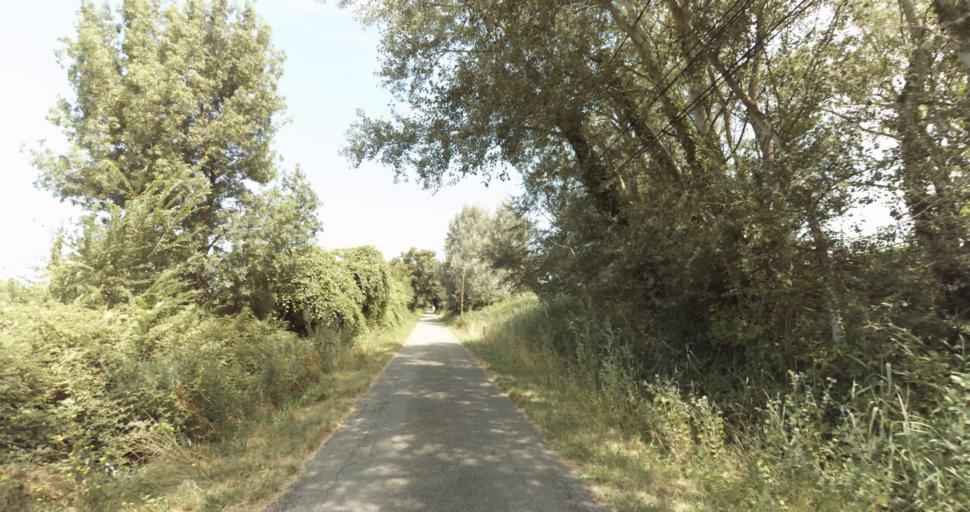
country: FR
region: Provence-Alpes-Cote d'Azur
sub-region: Departement du Vaucluse
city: Althen-des-Paluds
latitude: 44.0281
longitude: 4.9394
